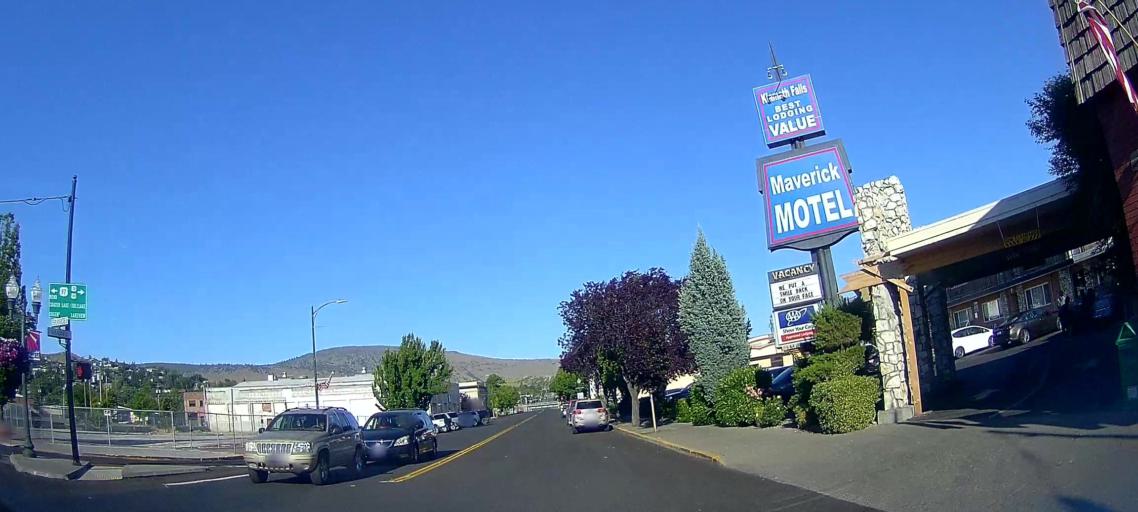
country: US
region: Oregon
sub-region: Klamath County
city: Klamath Falls
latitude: 42.2283
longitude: -121.7772
